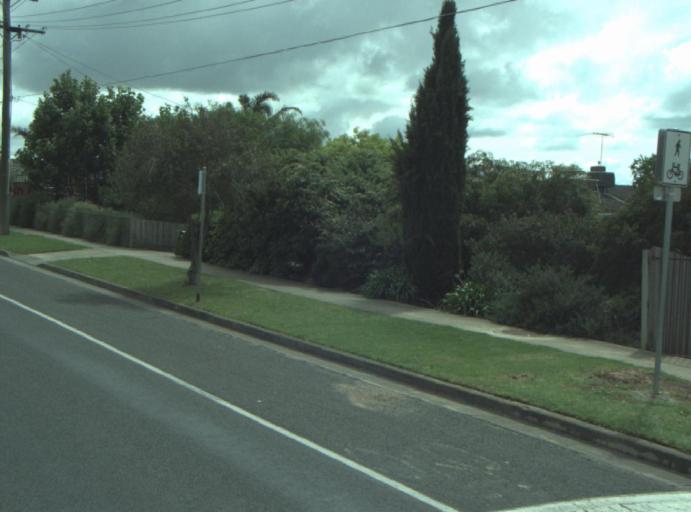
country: AU
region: Victoria
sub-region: Greater Geelong
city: Wandana Heights
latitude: -38.1851
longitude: 144.3104
